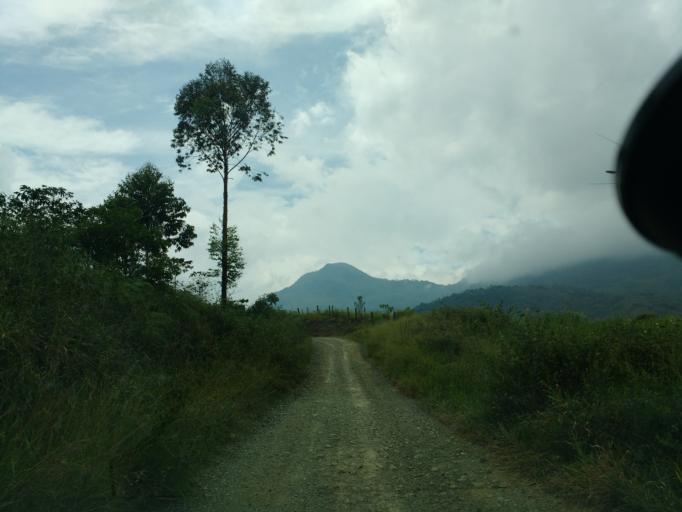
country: CO
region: Cauca
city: Santander de Quilichao
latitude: 2.9145
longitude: -76.4765
